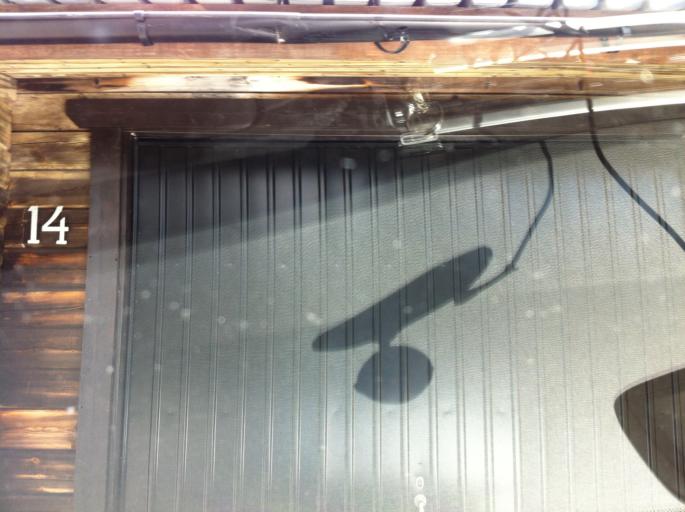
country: NO
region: Hedmark
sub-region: Engerdal
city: Engerdal
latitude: 62.5413
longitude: 12.4449
